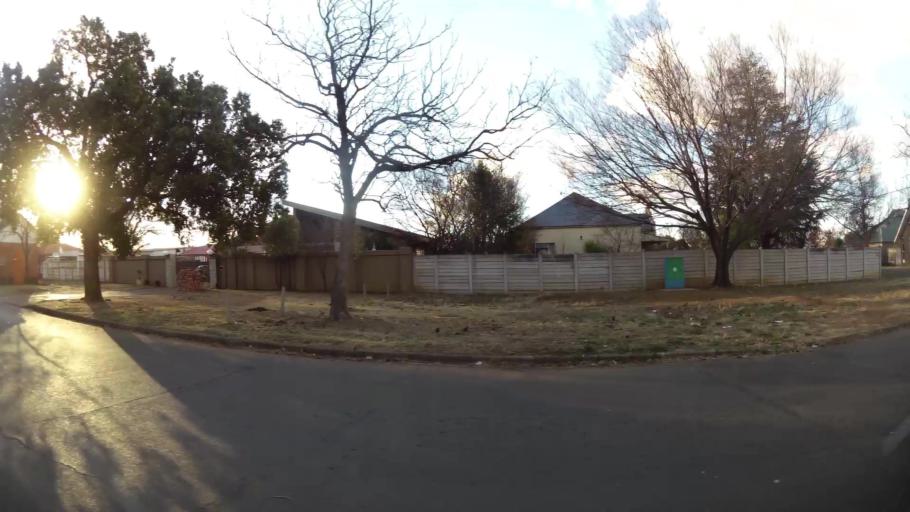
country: ZA
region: North-West
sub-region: Dr Kenneth Kaunda District Municipality
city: Potchefstroom
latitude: -26.7306
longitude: 27.0914
